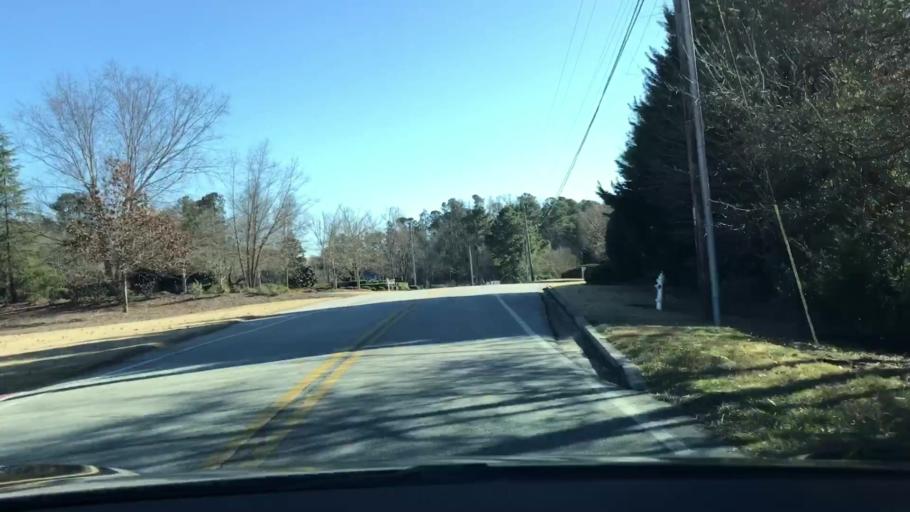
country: US
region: Georgia
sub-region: Gwinnett County
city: Buford
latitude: 34.1474
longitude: -84.0121
